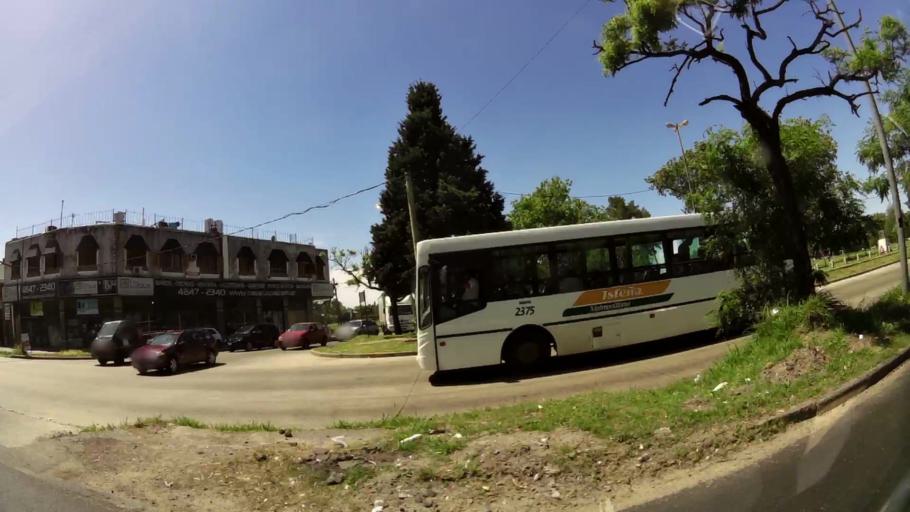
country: AR
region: Buenos Aires
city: Caseros
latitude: -34.5671
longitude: -58.5592
